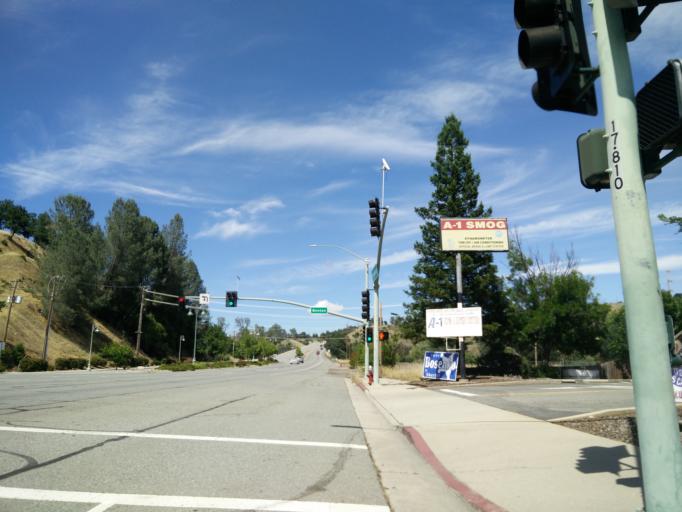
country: US
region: California
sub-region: Shasta County
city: Redding
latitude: 40.5992
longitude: -122.3842
